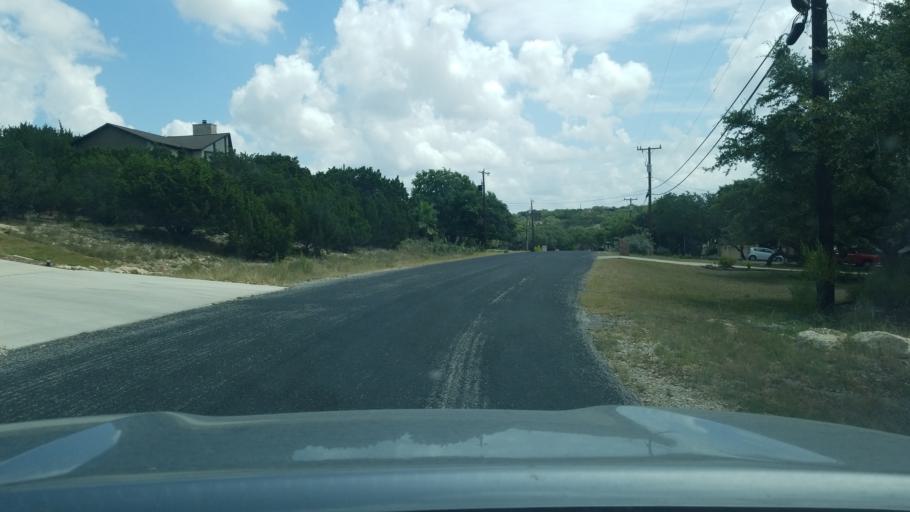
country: US
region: Texas
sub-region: Bexar County
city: Timberwood Park
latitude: 29.7007
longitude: -98.4934
